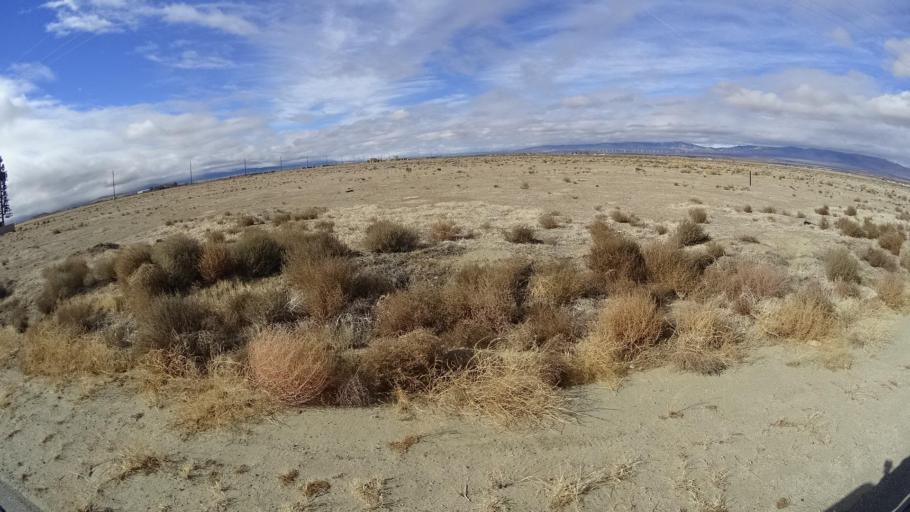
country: US
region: California
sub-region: Kern County
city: Rosamond
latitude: 34.8363
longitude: -118.2731
